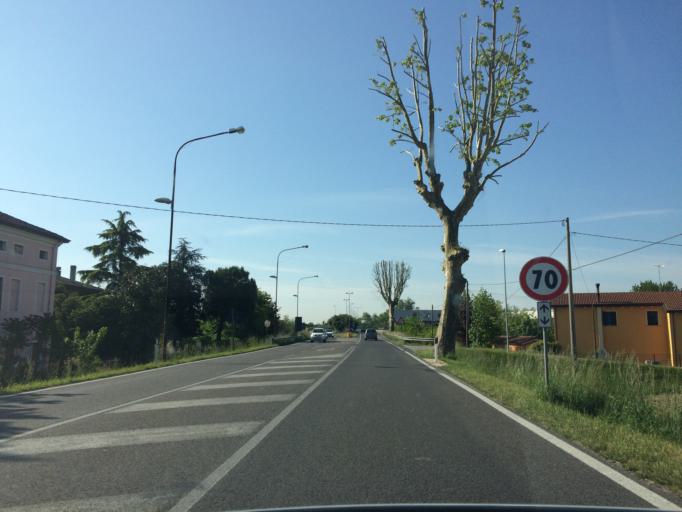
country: IT
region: Veneto
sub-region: Provincia di Padova
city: Curtarolo
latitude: 45.5206
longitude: 11.8316
